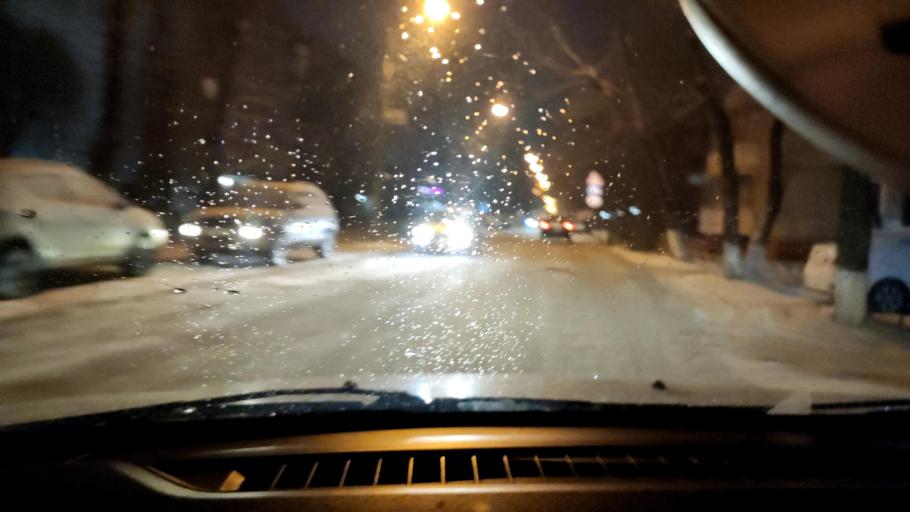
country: RU
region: Perm
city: Overyata
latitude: 58.0093
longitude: 55.9528
